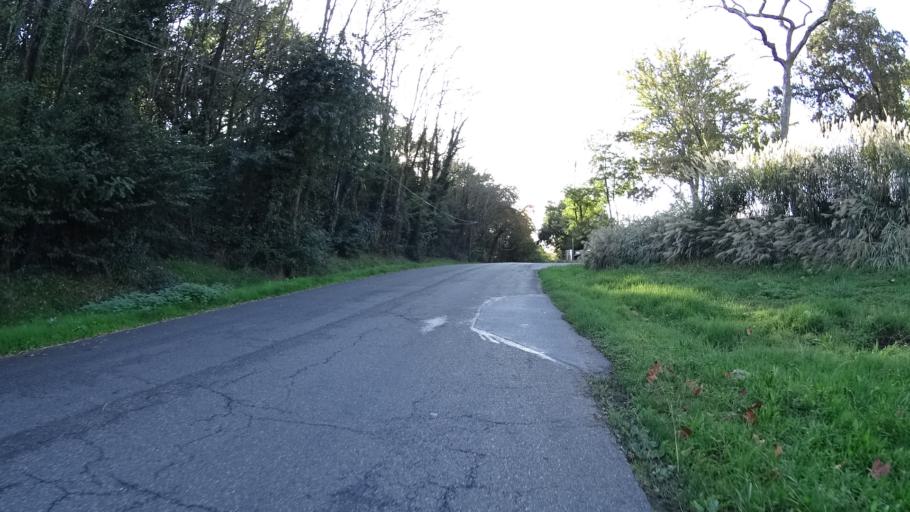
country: FR
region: Aquitaine
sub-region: Departement des Landes
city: Saint-Paul-les-Dax
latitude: 43.7382
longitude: -1.0441
